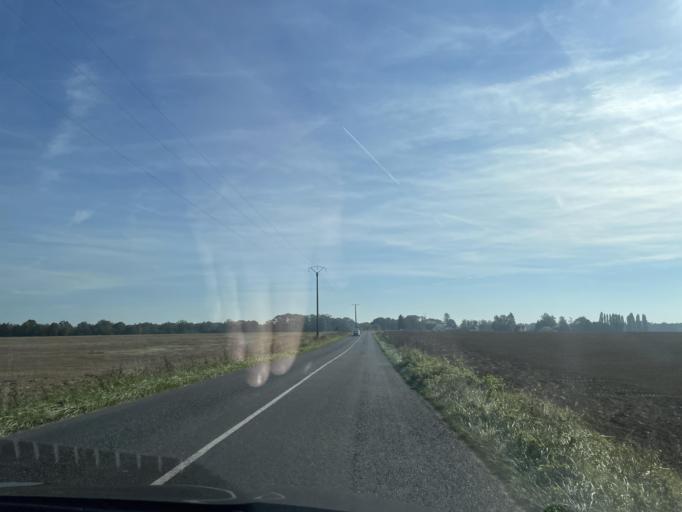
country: FR
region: Ile-de-France
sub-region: Departement de Seine-et-Marne
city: Sammeron
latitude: 48.9007
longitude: 3.0531
